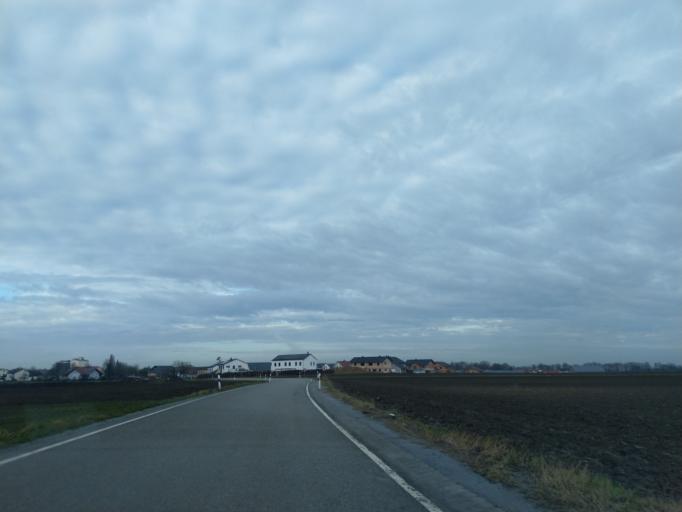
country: DE
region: Bavaria
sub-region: Lower Bavaria
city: Oberporing
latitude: 48.6986
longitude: 12.8337
